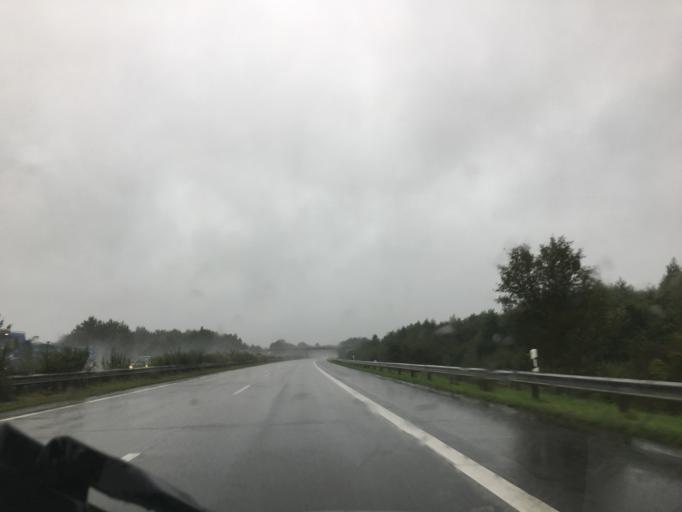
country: DE
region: Schleswig-Holstein
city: Mielkendorf
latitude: 54.2690
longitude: 10.0445
